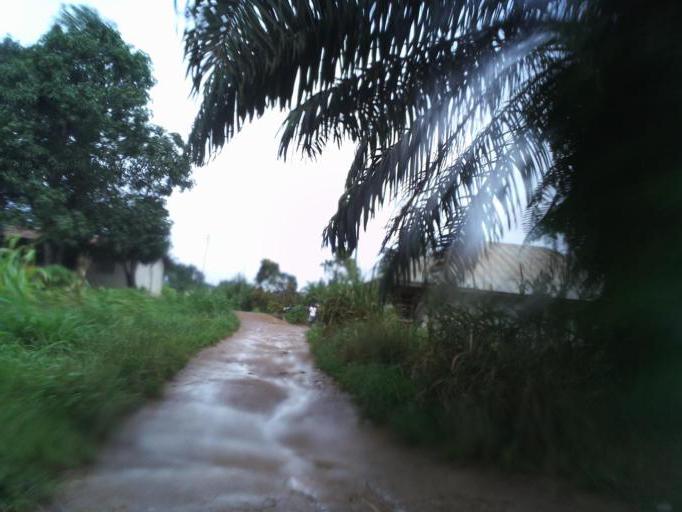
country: SL
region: Eastern Province
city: Kenema
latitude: 7.8493
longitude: -11.1955
